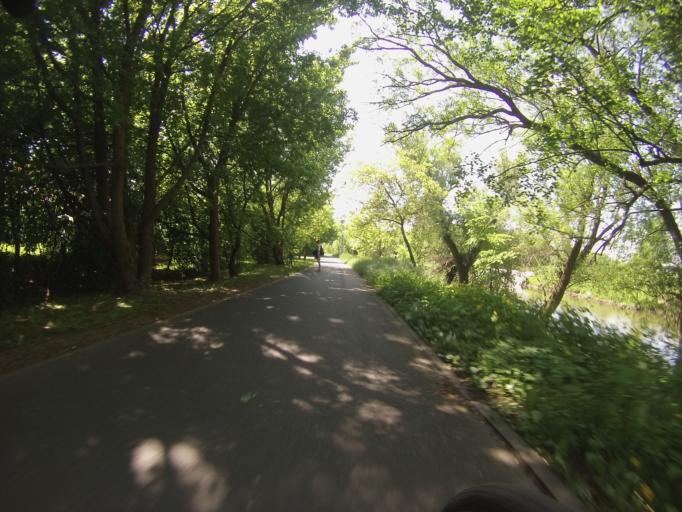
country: CZ
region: South Moravian
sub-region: Mesto Brno
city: Brno
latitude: 49.1660
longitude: 16.6234
